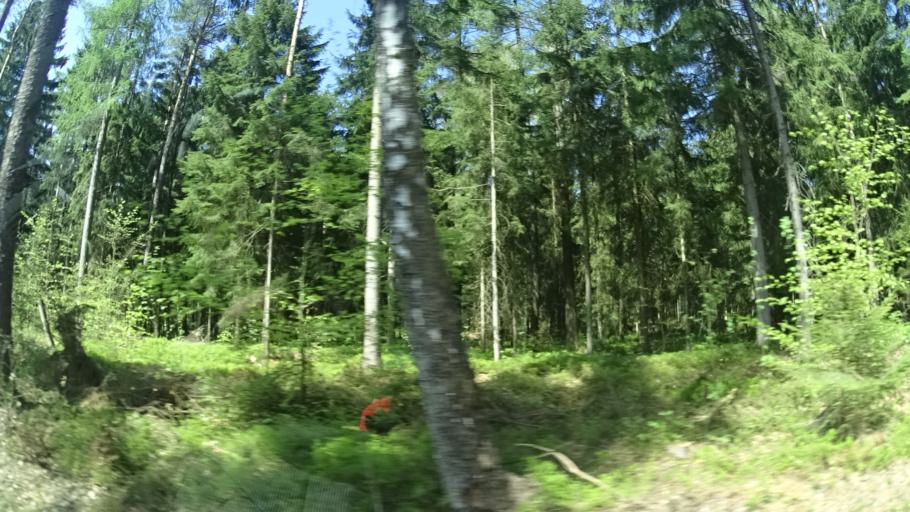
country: DE
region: Thuringia
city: Hildburghausen
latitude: 50.4431
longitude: 10.7583
